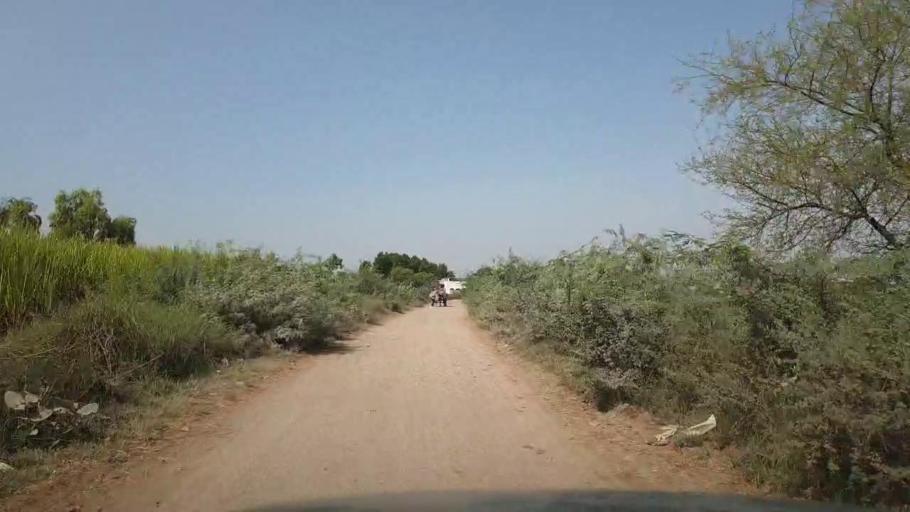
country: PK
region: Sindh
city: Tando Muhammad Khan
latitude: 25.1581
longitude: 68.3893
